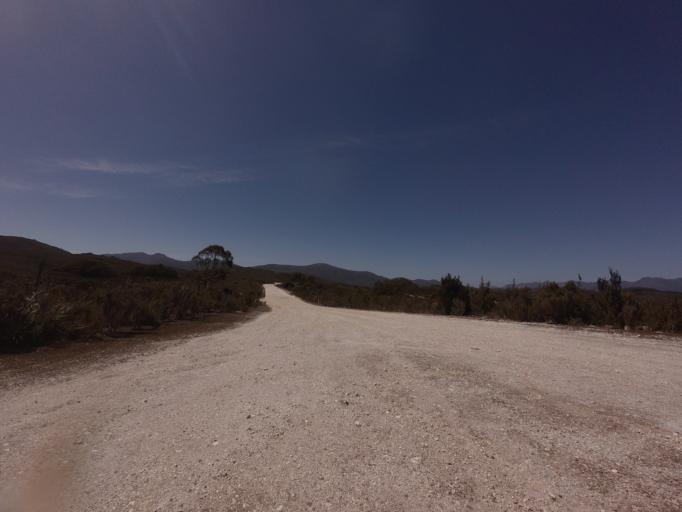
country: AU
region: Tasmania
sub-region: Huon Valley
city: Geeveston
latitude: -43.0308
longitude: 146.3019
